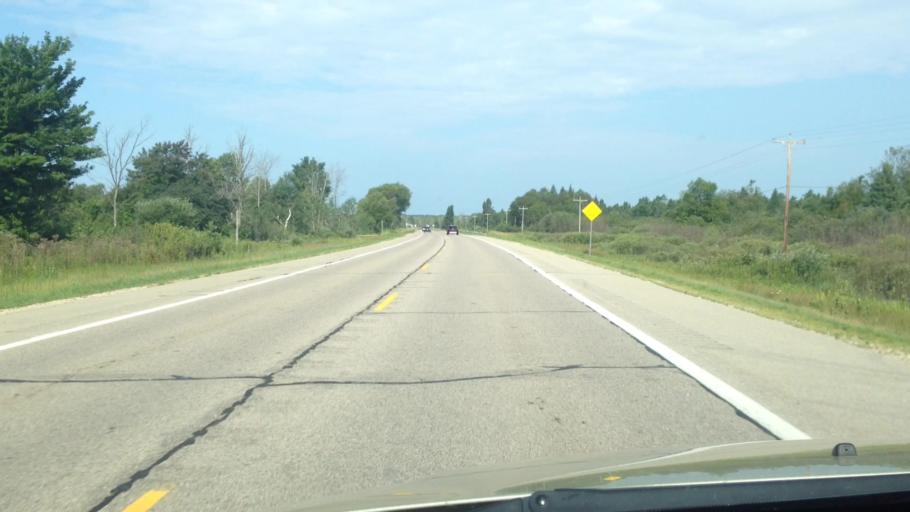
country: US
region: Michigan
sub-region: Schoolcraft County
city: Manistique
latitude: 45.9004
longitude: -86.5629
